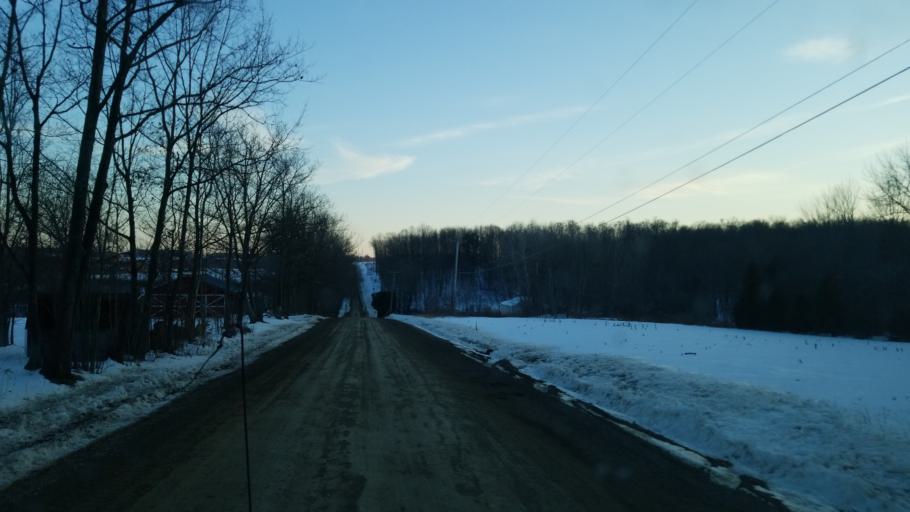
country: US
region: Pennsylvania
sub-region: Tioga County
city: Westfield
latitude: 42.0377
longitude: -77.6198
